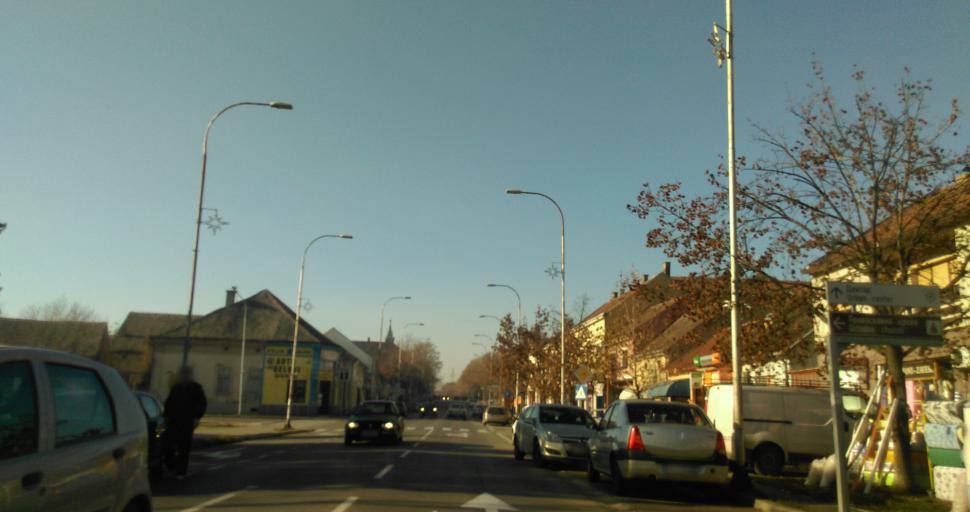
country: RS
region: Autonomna Pokrajina Vojvodina
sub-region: Sremski Okrug
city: Ruma
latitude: 45.0074
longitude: 19.8296
